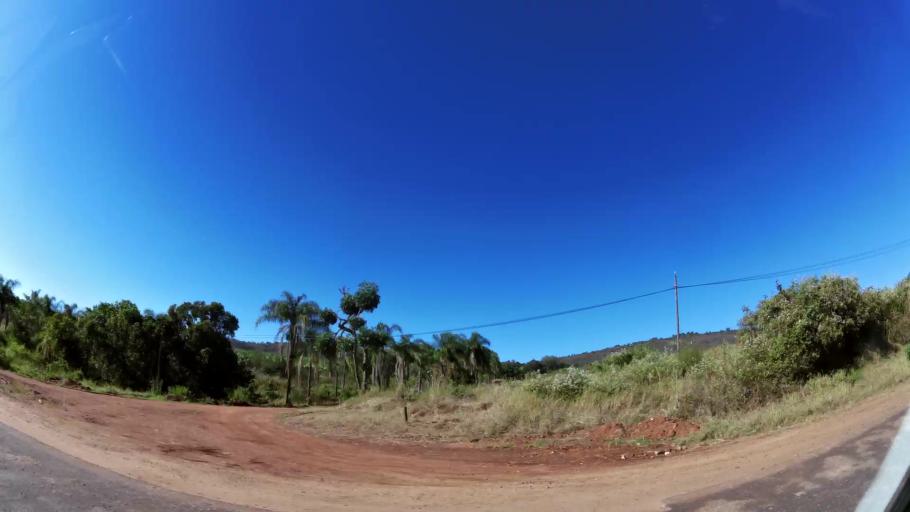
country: ZA
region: Limpopo
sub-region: Mopani District Municipality
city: Tzaneen
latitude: -23.8429
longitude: 30.1938
